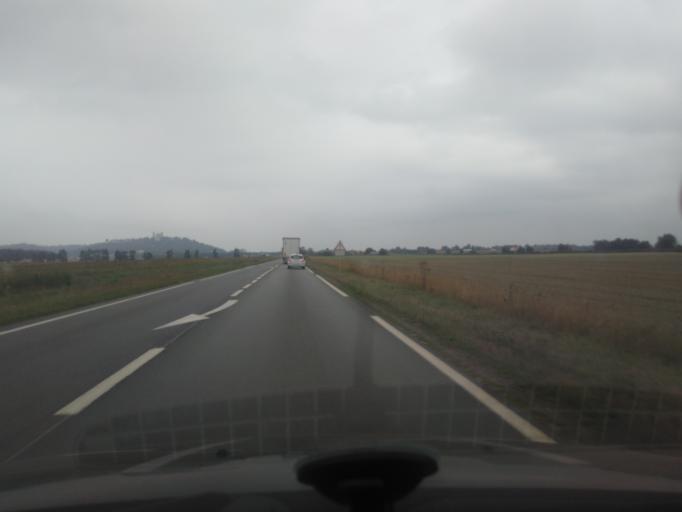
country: FR
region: Picardie
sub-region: Departement de l'Aisne
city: Athies-sous-Laon
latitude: 49.5644
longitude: 3.6762
